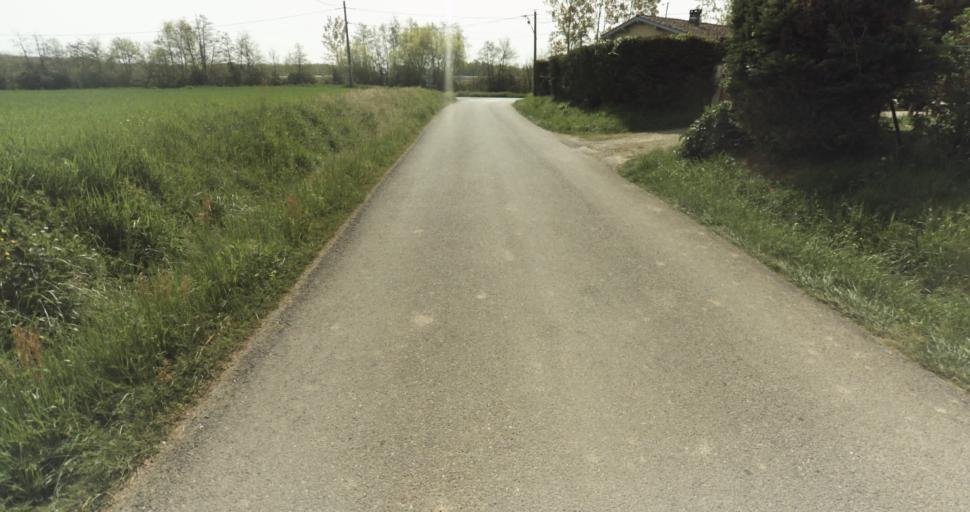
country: FR
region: Midi-Pyrenees
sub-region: Departement du Tarn-et-Garonne
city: Moissac
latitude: 44.0784
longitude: 1.0773
